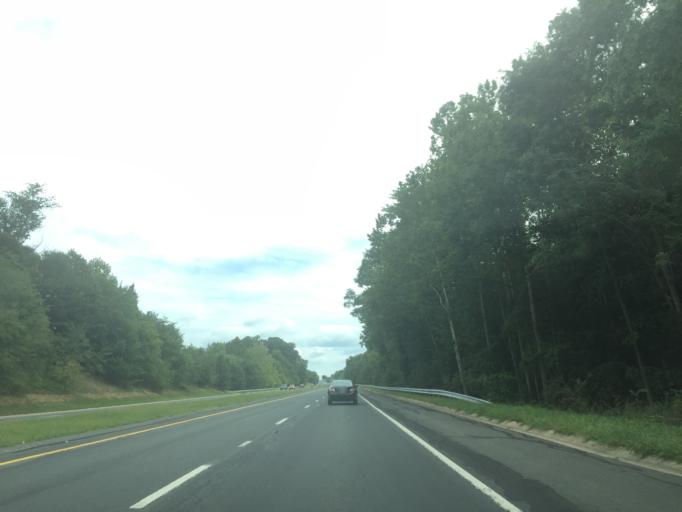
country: US
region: Maryland
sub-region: Montgomery County
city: Gaithersburg
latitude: 39.1558
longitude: -77.1821
